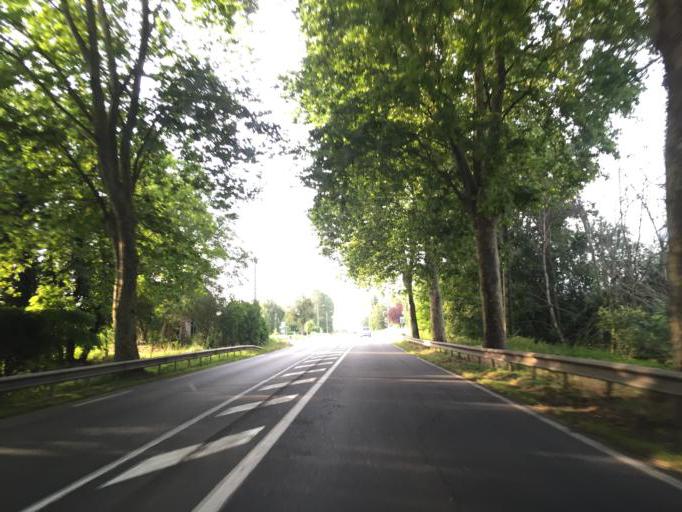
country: FR
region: Auvergne
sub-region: Departement de l'Allier
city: Varennes-sur-Allier
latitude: 46.3401
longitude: 3.3823
